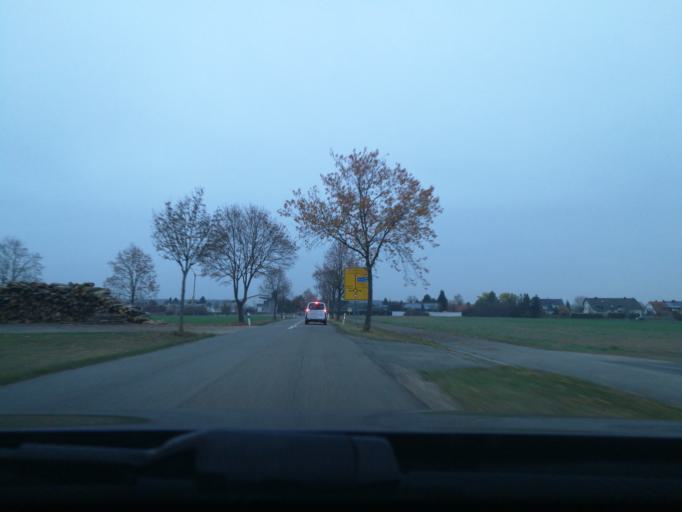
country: DE
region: Bavaria
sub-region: Regierungsbezirk Mittelfranken
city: Obermichelbach
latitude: 49.5231
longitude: 10.9126
